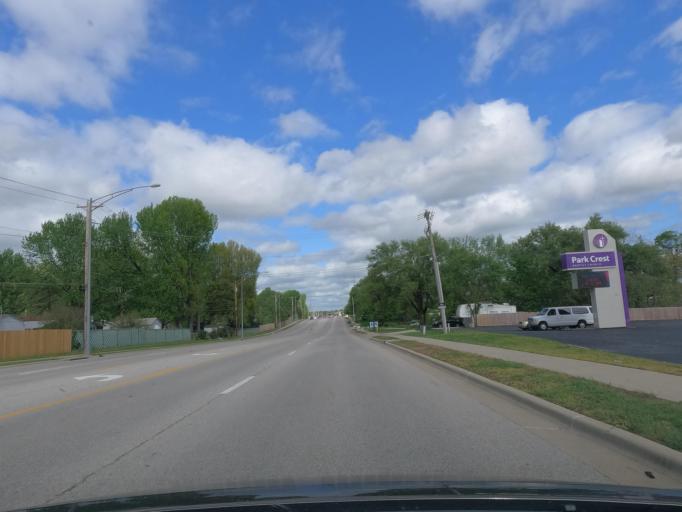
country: US
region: Missouri
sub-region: Greene County
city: Battlefield
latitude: 37.1382
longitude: -93.3030
